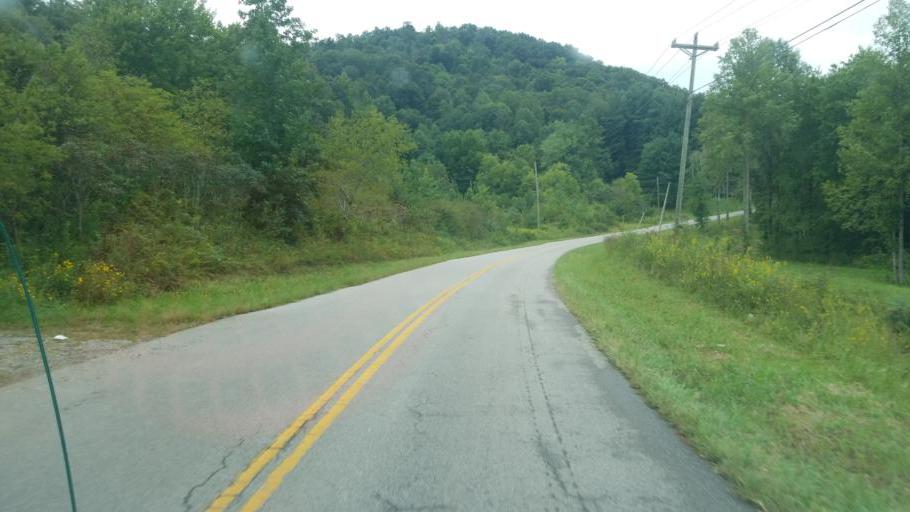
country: US
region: Kentucky
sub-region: Rowan County
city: Morehead
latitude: 38.3169
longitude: -83.5513
